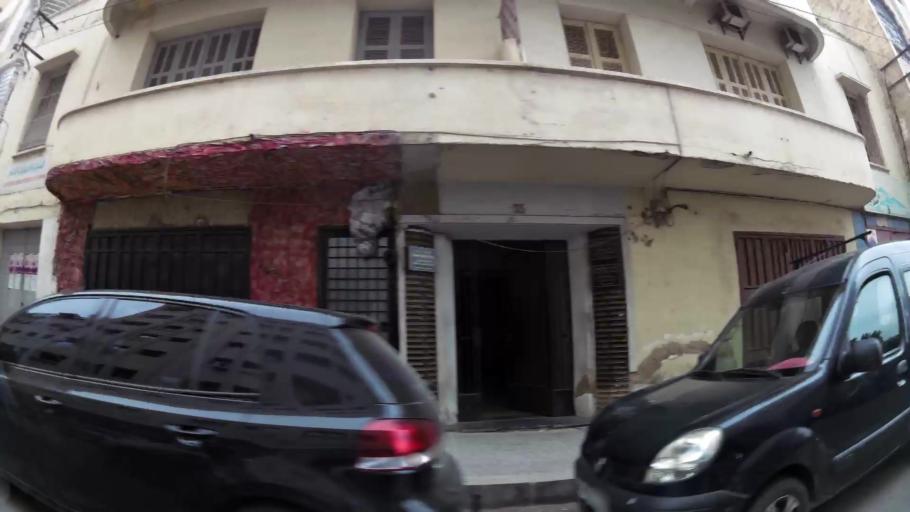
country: MA
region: Fes-Boulemane
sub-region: Fes
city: Fes
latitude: 34.0458
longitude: -5.0037
